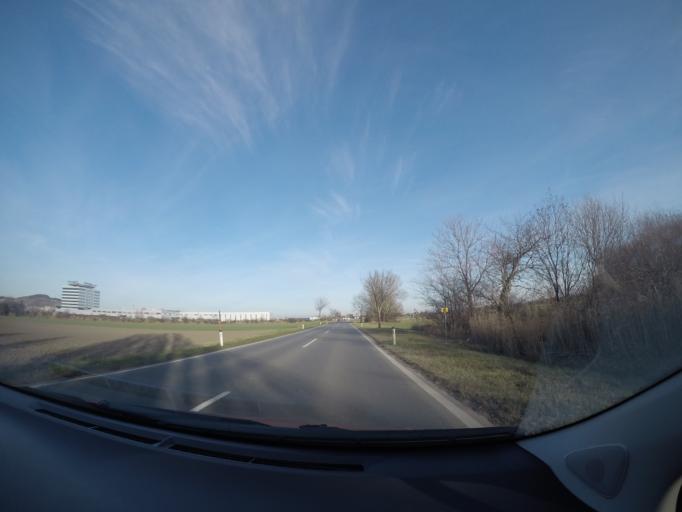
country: AT
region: Lower Austria
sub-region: Politischer Bezirk Baden
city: Traiskirchen
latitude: 48.0318
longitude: 16.2936
